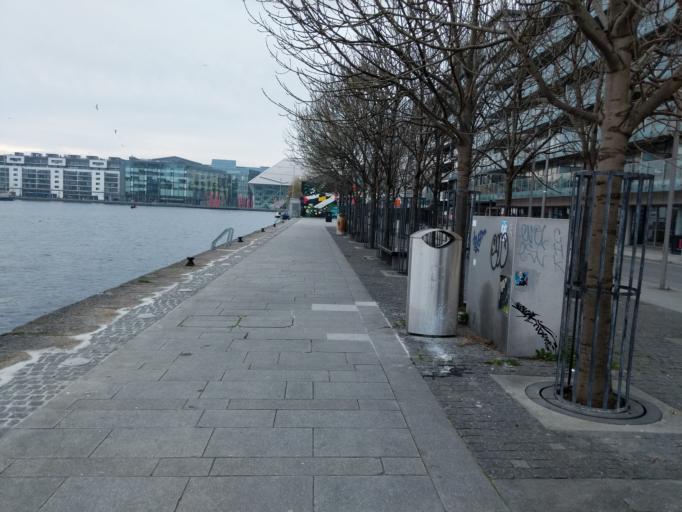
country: IE
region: Leinster
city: Ringsend
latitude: 53.3439
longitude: -6.2337
